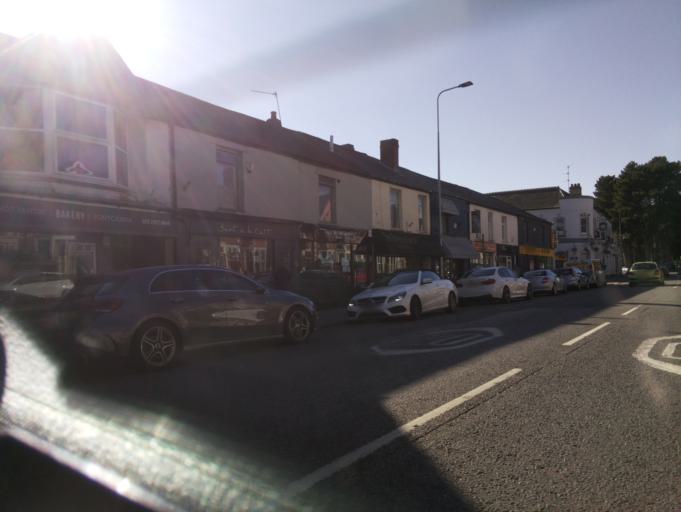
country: GB
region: Wales
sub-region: Cardiff
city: Cardiff
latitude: 51.4890
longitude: -3.2014
